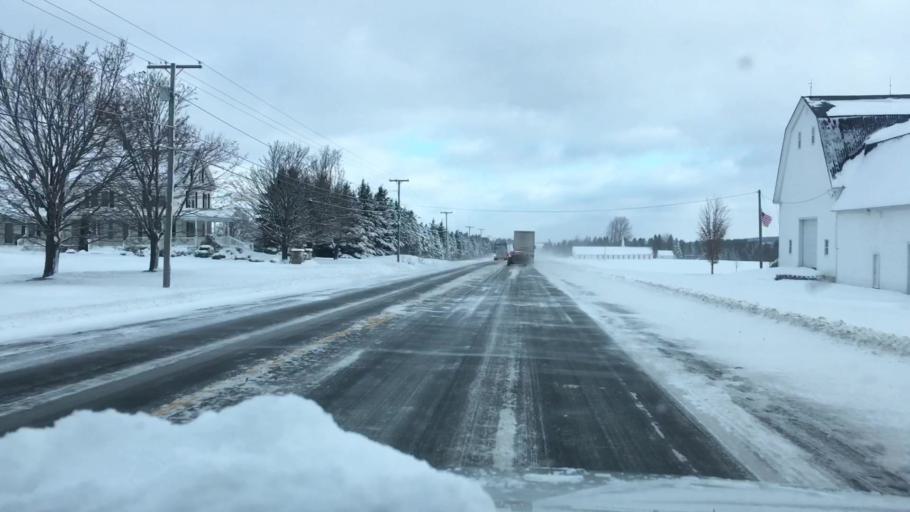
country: US
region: Maine
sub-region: Aroostook County
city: Presque Isle
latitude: 46.7324
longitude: -68.0011
